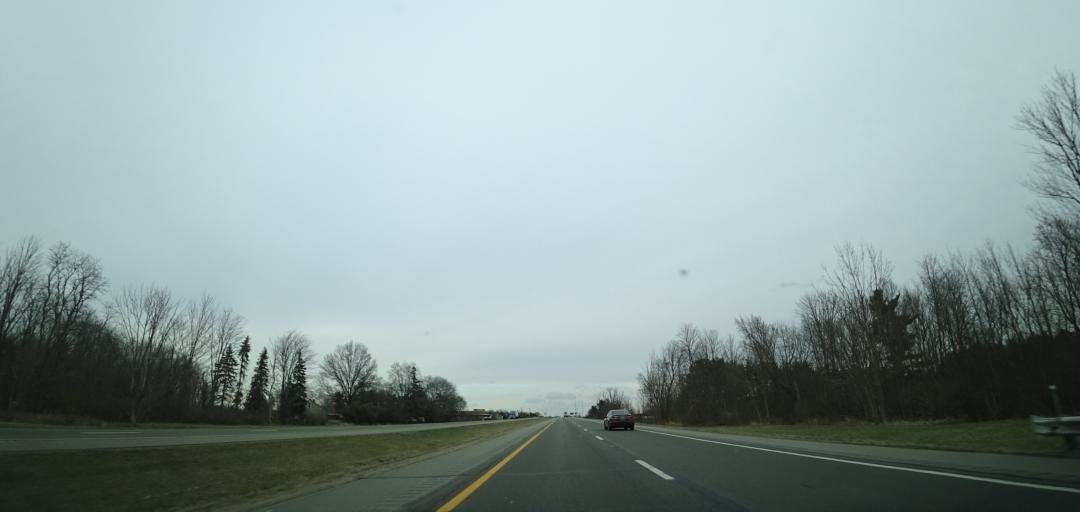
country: US
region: Ohio
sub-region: Mahoning County
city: Boardman
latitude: 40.9733
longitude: -80.6661
